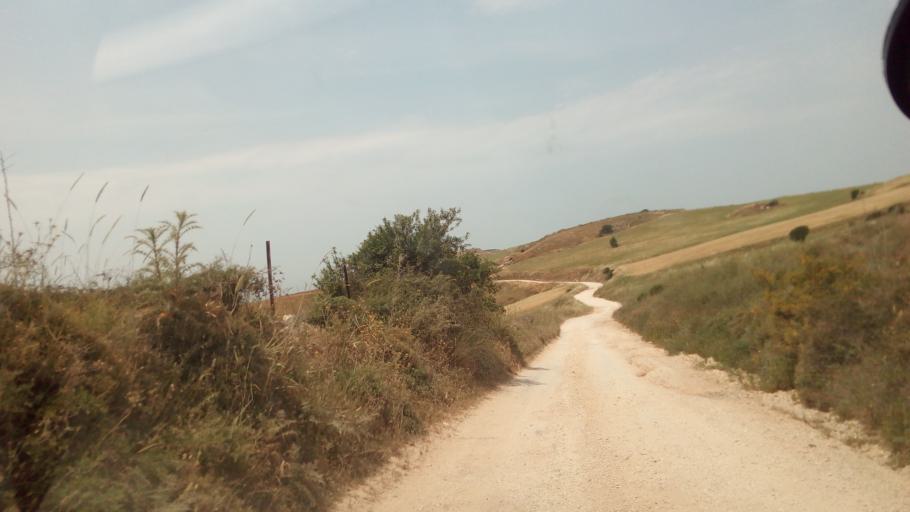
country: CY
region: Pafos
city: Polis
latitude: 34.9744
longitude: 32.3712
